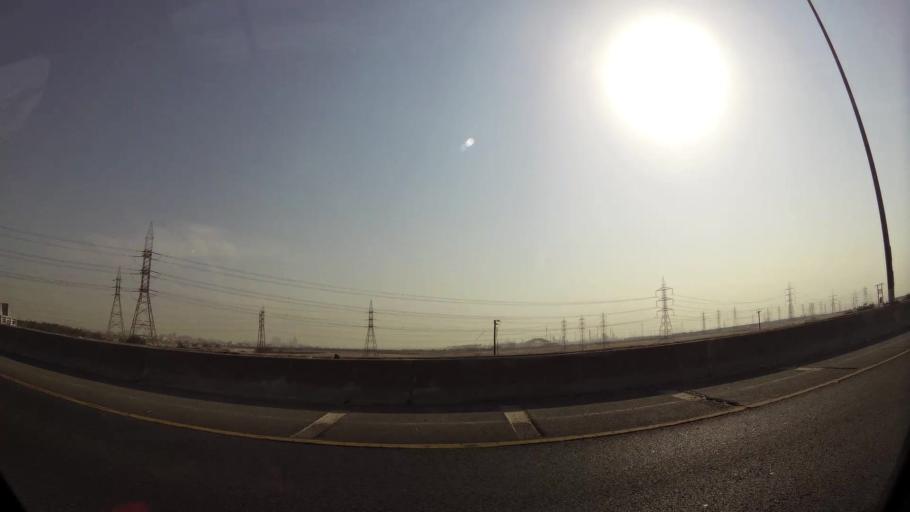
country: KW
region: Al Ahmadi
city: Al Ahmadi
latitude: 29.0697
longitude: 48.0990
